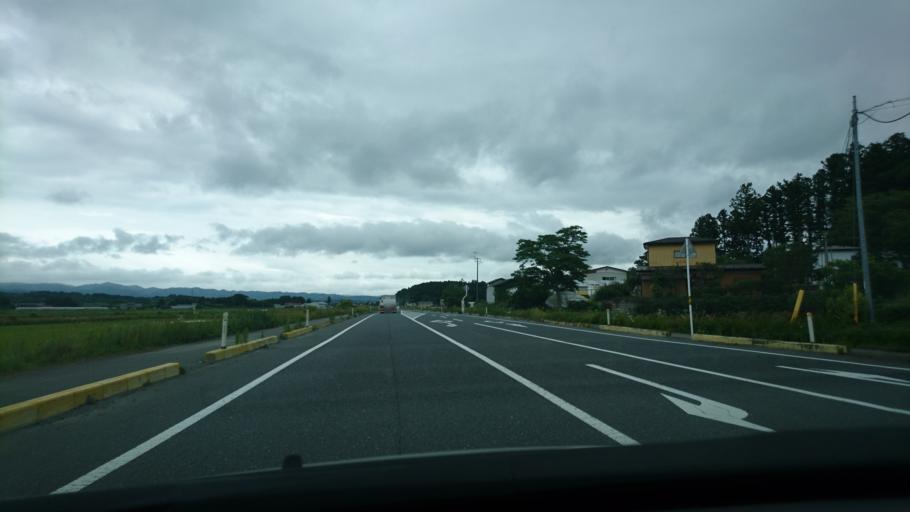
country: JP
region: Iwate
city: Ichinoseki
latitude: 38.7400
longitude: 141.2561
